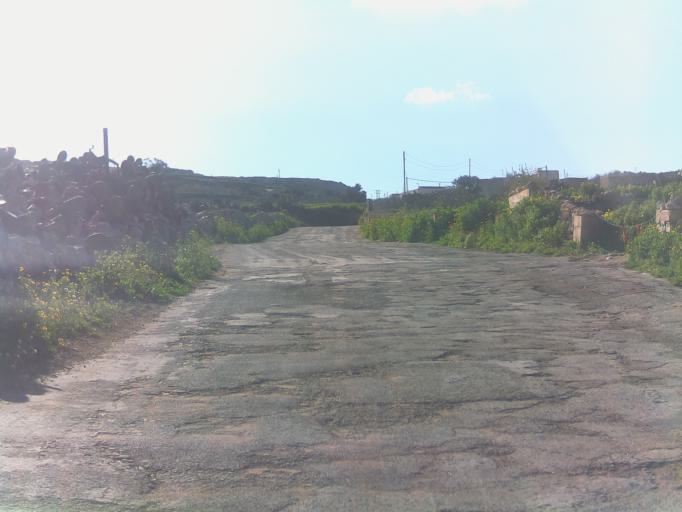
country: MT
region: L-Imgarr
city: Imgarr
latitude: 35.9086
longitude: 14.3566
